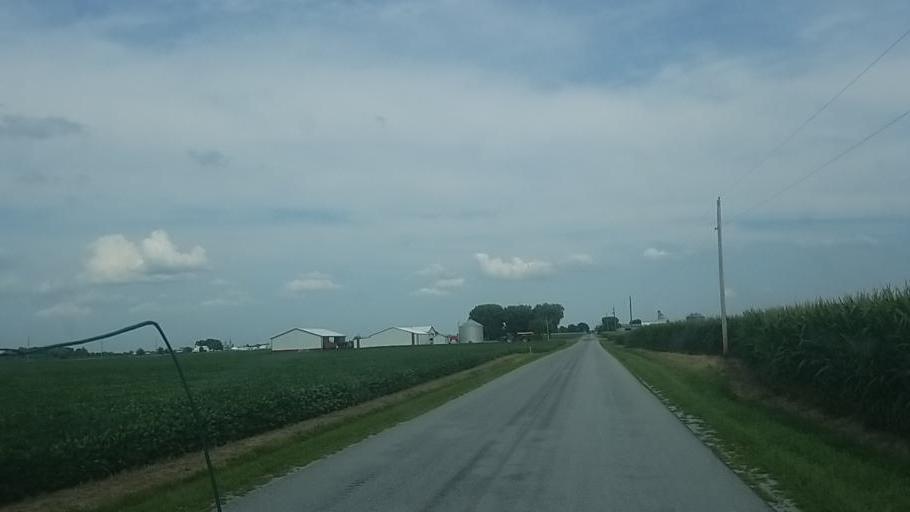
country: US
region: Ohio
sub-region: Wyandot County
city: Upper Sandusky
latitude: 40.8178
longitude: -83.3327
